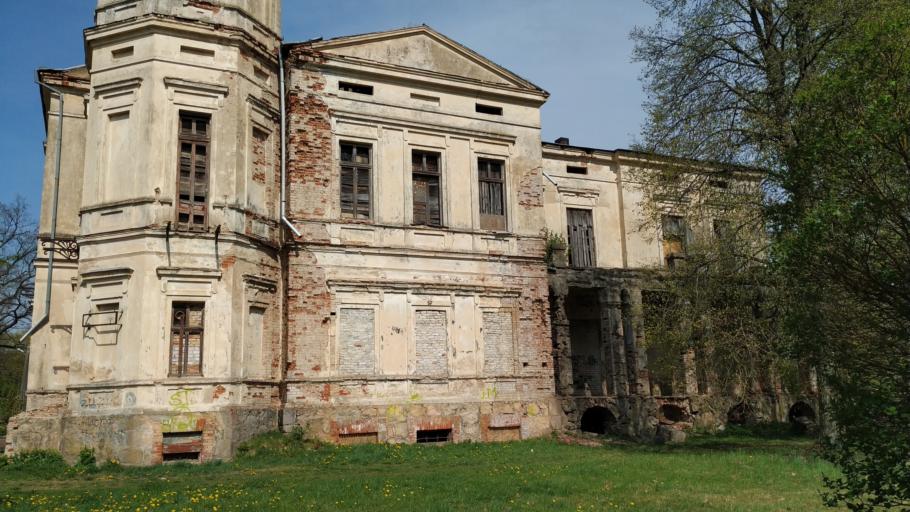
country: LT
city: Baltoji Voke
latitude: 54.5982
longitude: 25.1893
